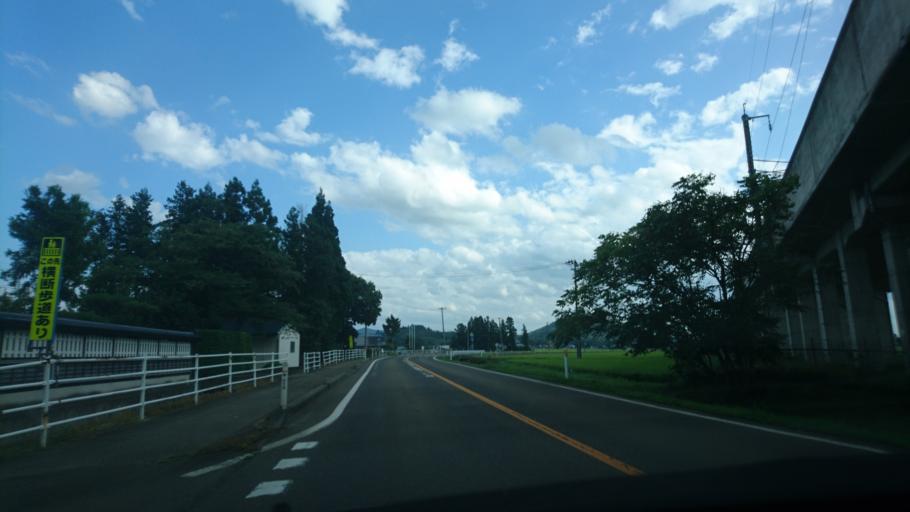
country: JP
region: Iwate
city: Hanamaki
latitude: 39.4931
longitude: 141.1741
